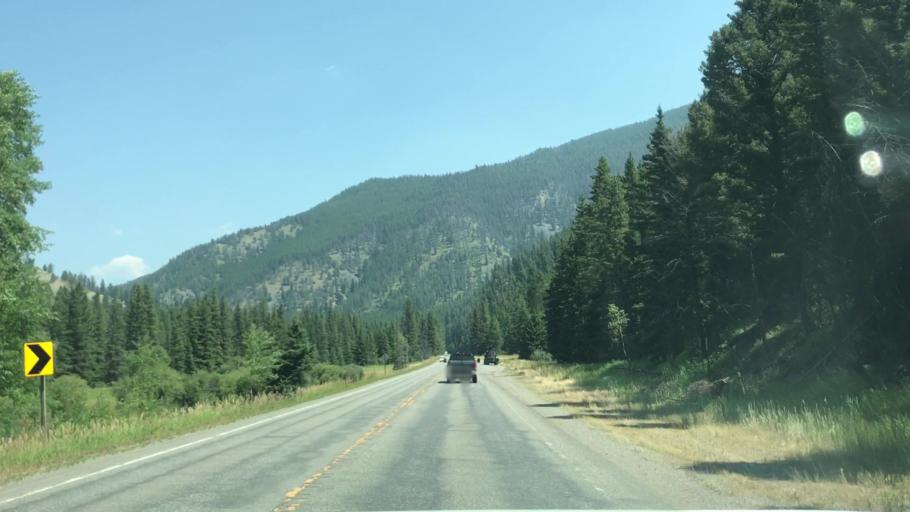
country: US
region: Montana
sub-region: Gallatin County
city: Big Sky
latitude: 45.2963
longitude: -111.2127
